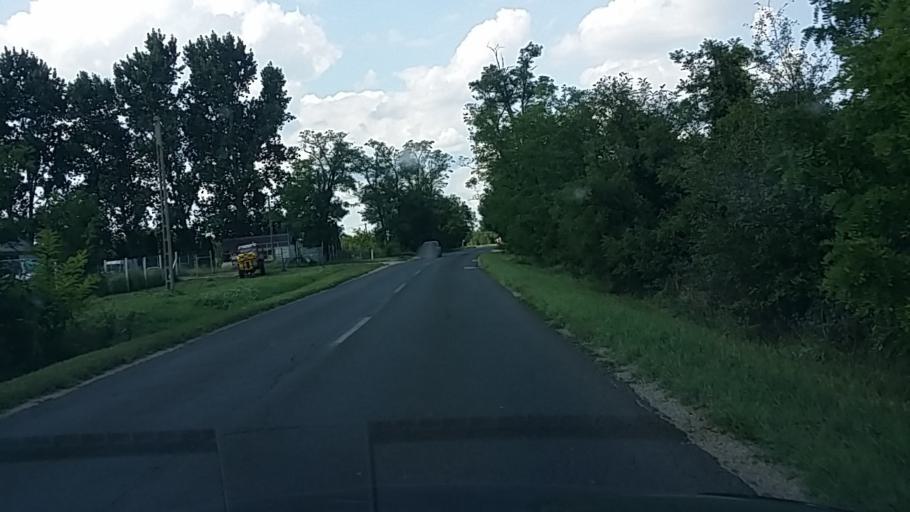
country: HU
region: Pest
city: Toekoel
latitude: 47.2977
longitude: 18.9787
